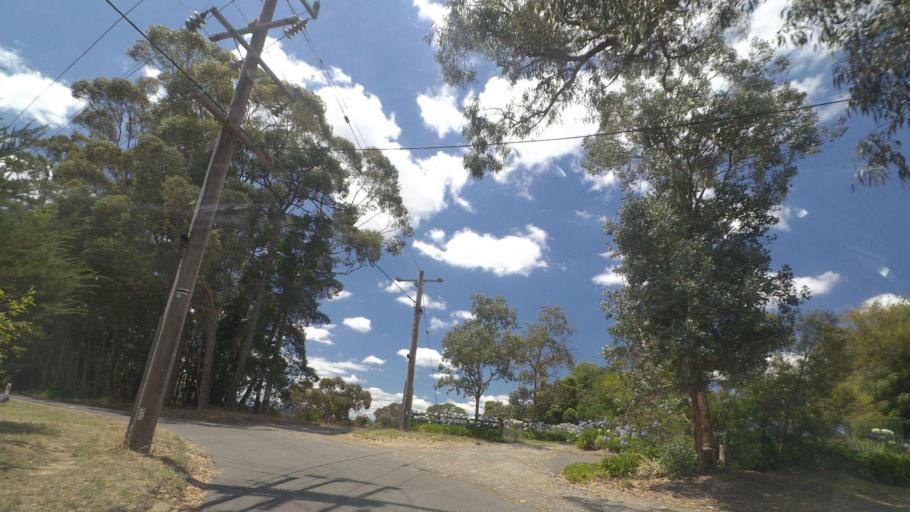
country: AU
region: Victoria
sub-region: Yarra Ranges
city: Chirnside Park
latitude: -37.7263
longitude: 145.2791
